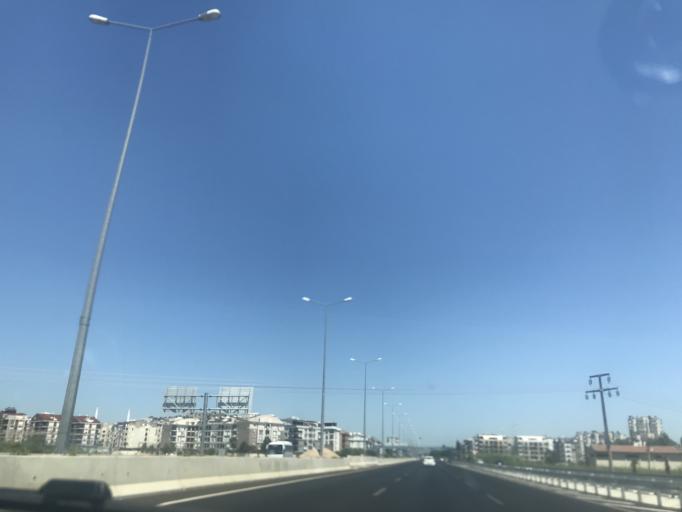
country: TR
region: Antalya
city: Cakirlar
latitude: 36.8490
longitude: 30.6021
